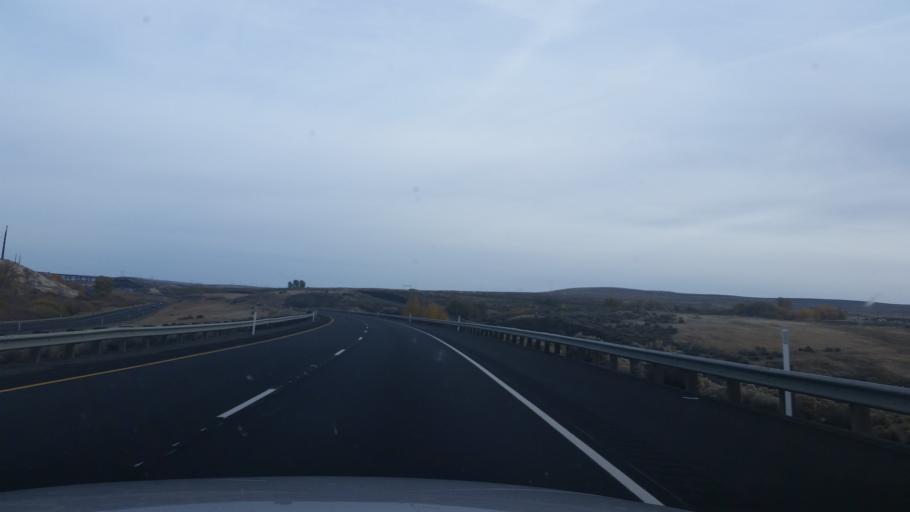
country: US
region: Washington
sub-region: Kittitas County
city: Kittitas
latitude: 46.9618
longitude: -120.3297
